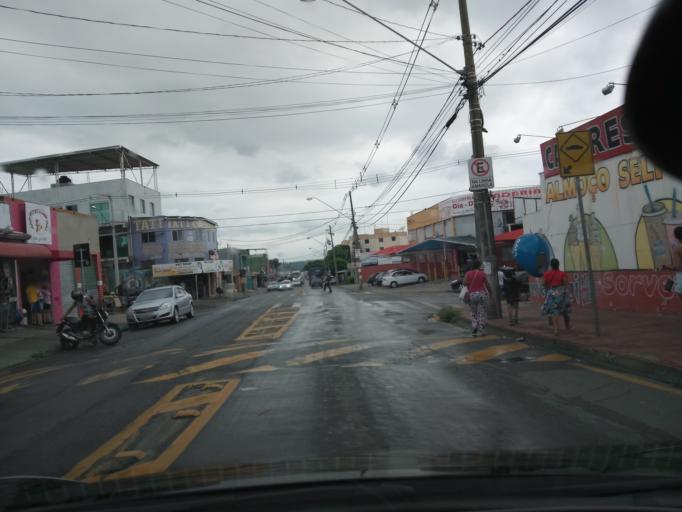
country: BR
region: Sao Paulo
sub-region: Campinas
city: Campinas
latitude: -22.9826
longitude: -47.1208
